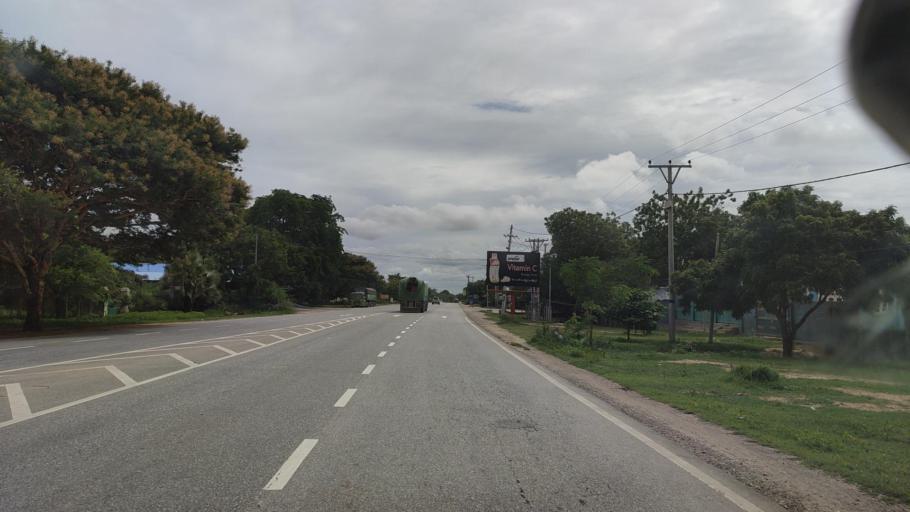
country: MM
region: Mandalay
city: Meiktila
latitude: 21.0557
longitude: 96.0010
